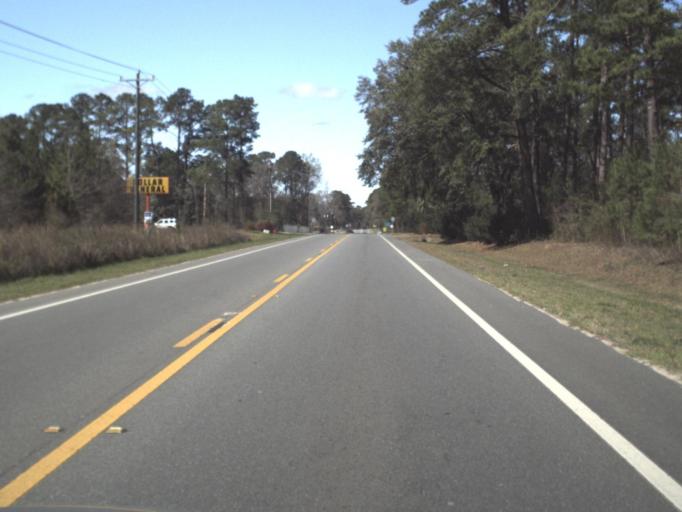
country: US
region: Florida
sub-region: Gadsden County
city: Gretna
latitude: 30.6026
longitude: -84.6529
